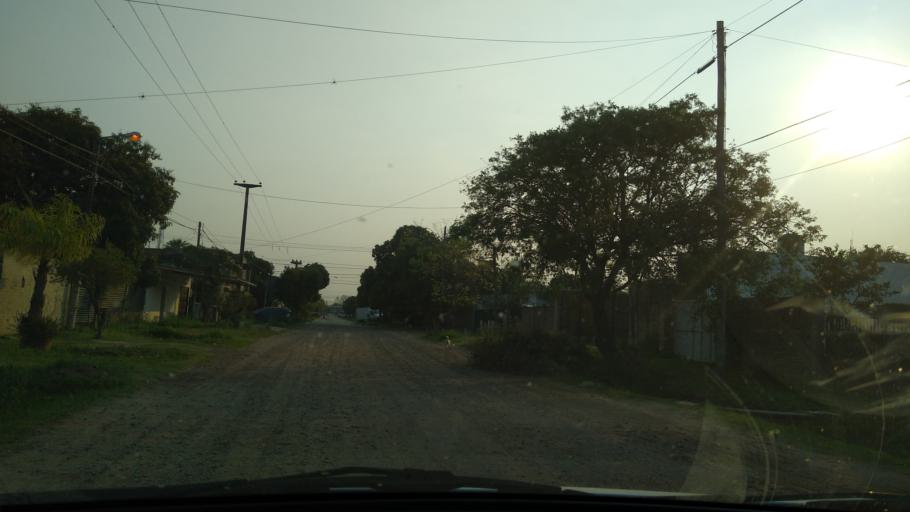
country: AR
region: Chaco
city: Barranqueras
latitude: -27.4868
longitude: -58.9440
